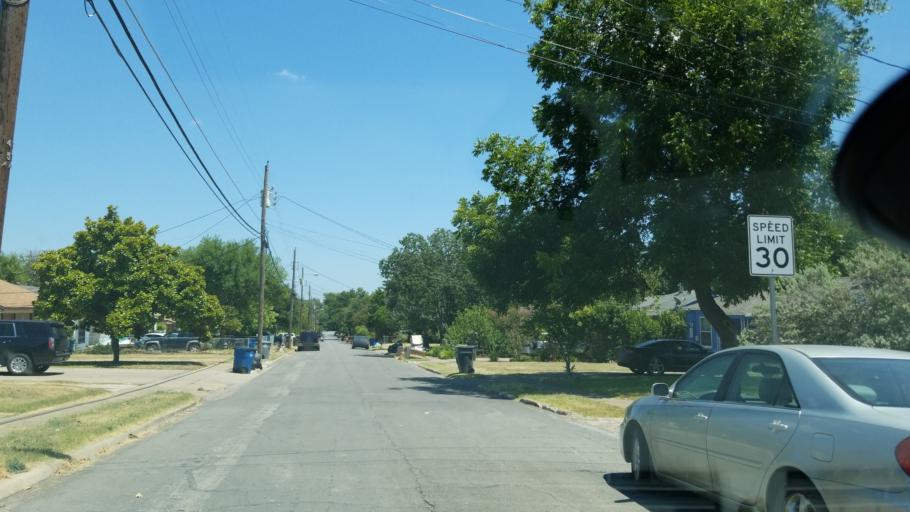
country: US
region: Texas
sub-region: Dallas County
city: Cockrell Hill
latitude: 32.7293
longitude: -96.8819
